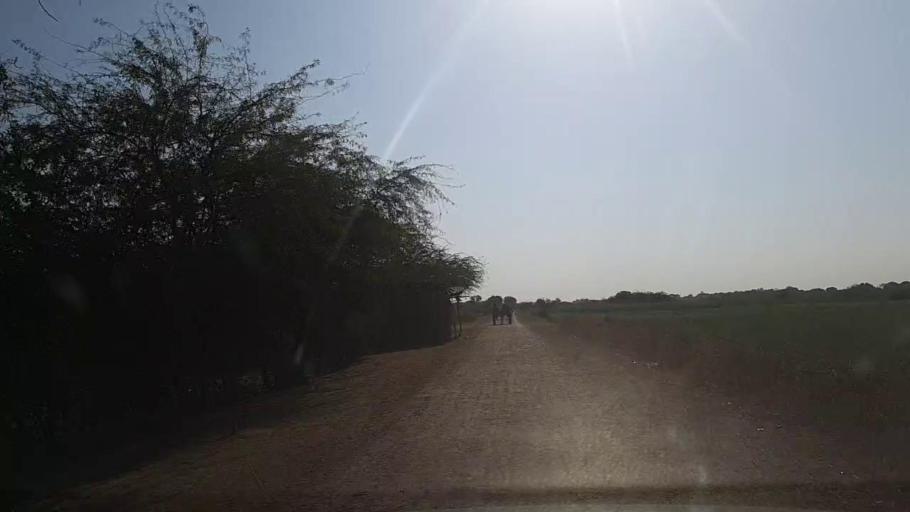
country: PK
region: Sindh
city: Digri
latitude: 25.0352
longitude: 69.2200
